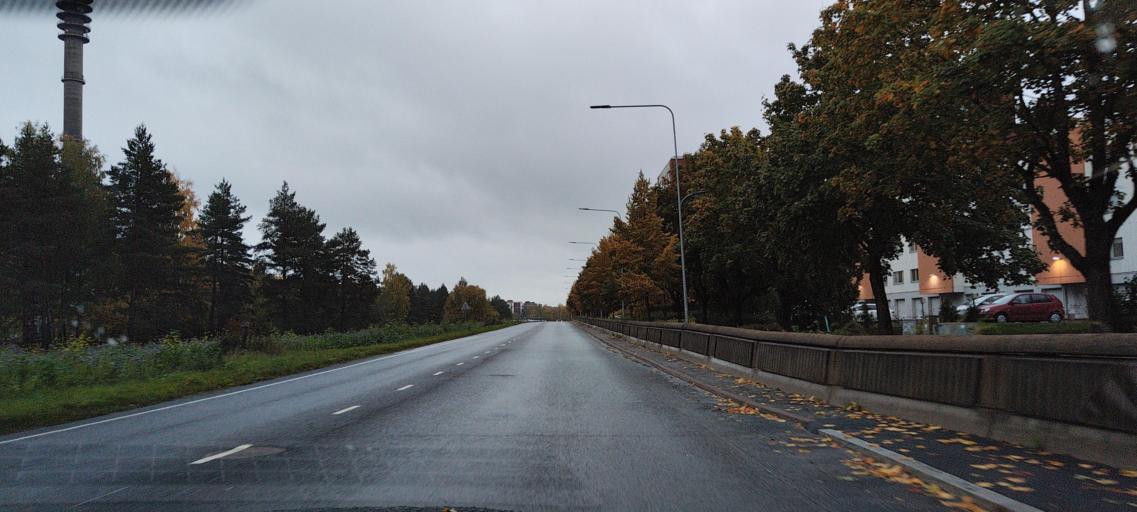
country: FI
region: Varsinais-Suomi
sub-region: Turku
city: Kaarina
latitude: 60.4505
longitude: 22.3306
